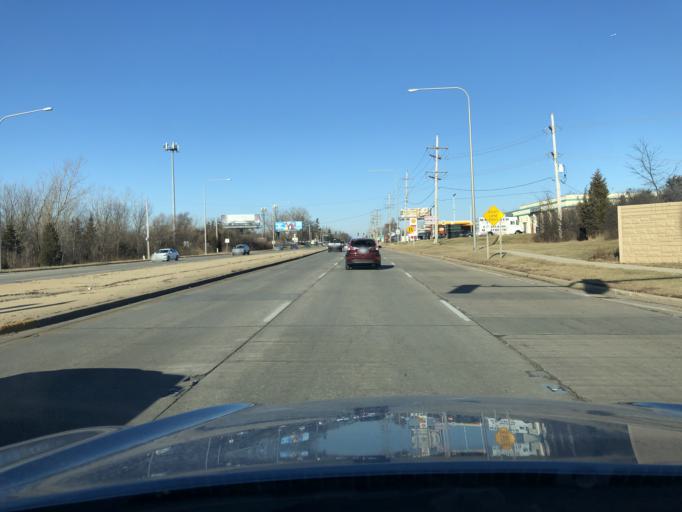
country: US
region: Illinois
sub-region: DuPage County
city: Roselle
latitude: 41.9951
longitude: -88.0801
